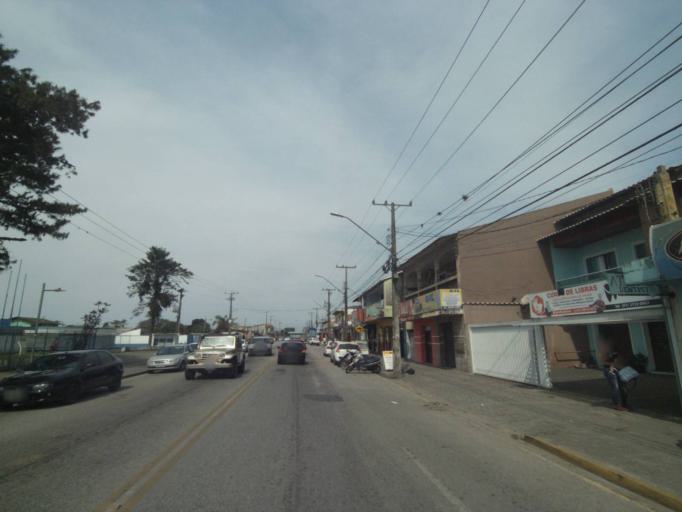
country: BR
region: Parana
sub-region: Paranagua
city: Paranagua
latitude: -25.5231
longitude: -48.5307
